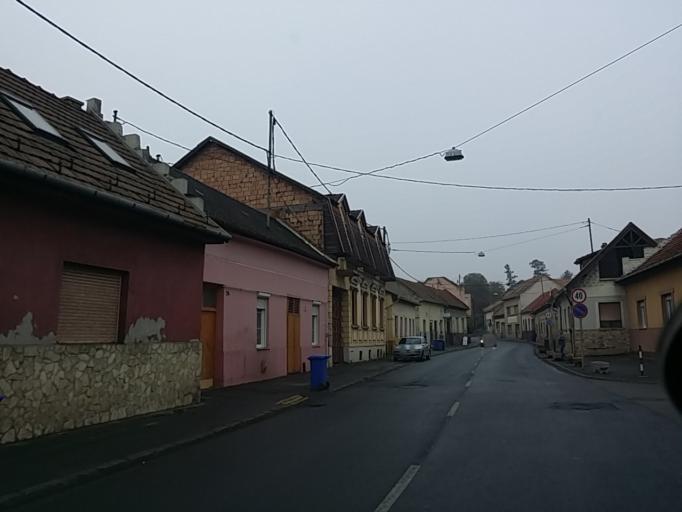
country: HU
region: Heves
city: Gyongyos
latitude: 47.7868
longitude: 19.9219
